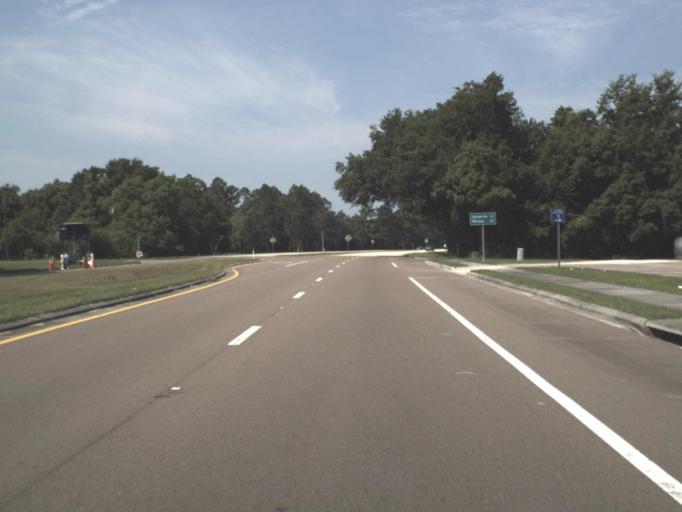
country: US
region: Florida
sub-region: Alachua County
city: Waldo
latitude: 29.7868
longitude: -82.1725
